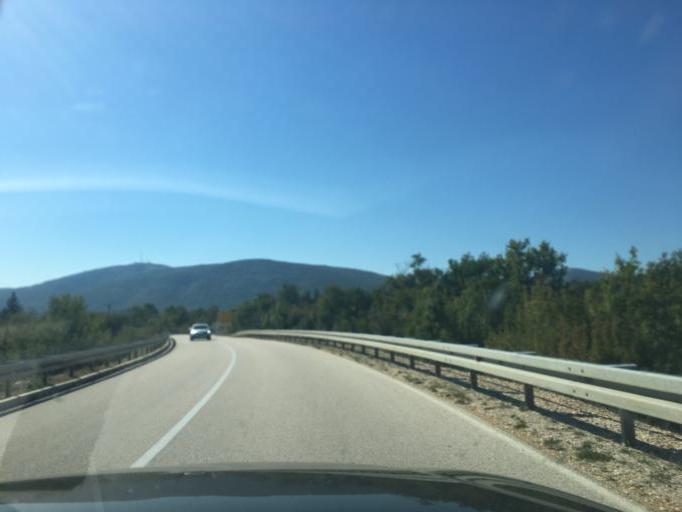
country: HR
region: Splitsko-Dalmatinska
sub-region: Grad Trogir
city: Trogir
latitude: 43.6121
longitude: 16.2248
